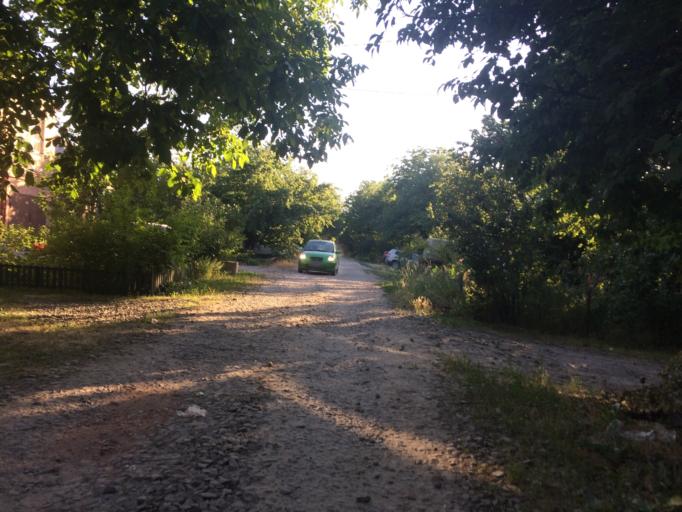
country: RU
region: Rostov
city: Rostov-na-Donu
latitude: 47.2164
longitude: 39.6431
